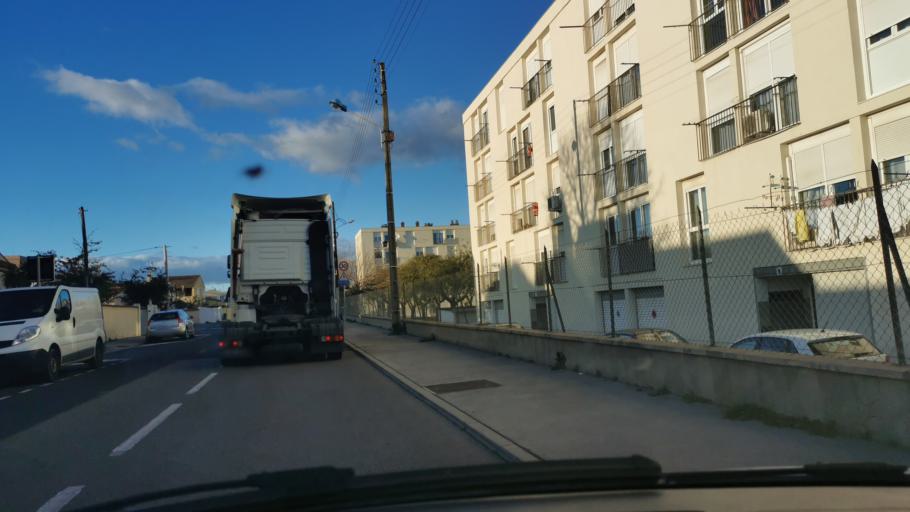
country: FR
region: Languedoc-Roussillon
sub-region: Departement de l'Herault
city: Frontignan
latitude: 43.4290
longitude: 3.7260
